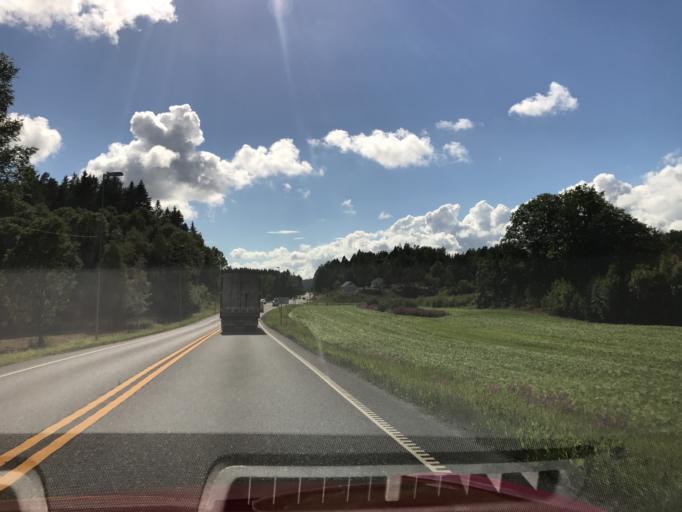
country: NO
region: Telemark
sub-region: Bamble
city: Herre
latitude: 58.9727
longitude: 9.5756
